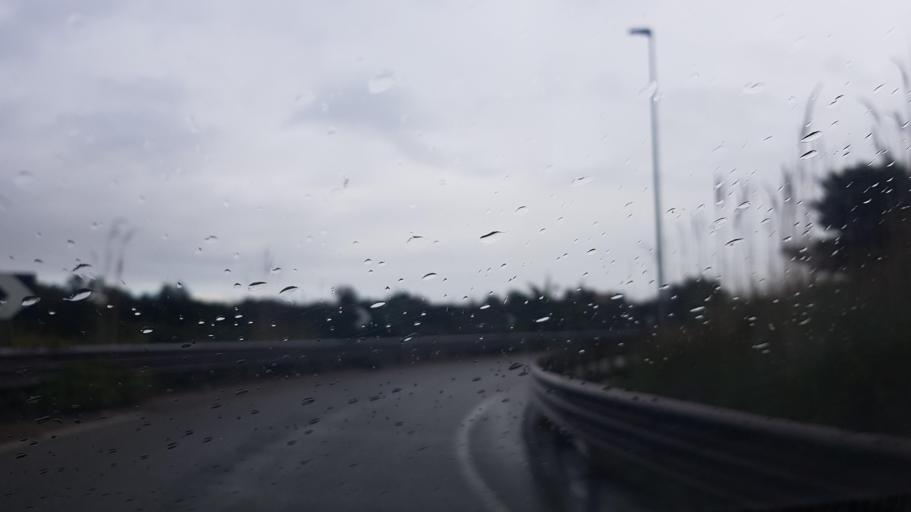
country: IT
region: Apulia
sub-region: Provincia di Taranto
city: Statte
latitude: 40.4858
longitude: 17.2068
